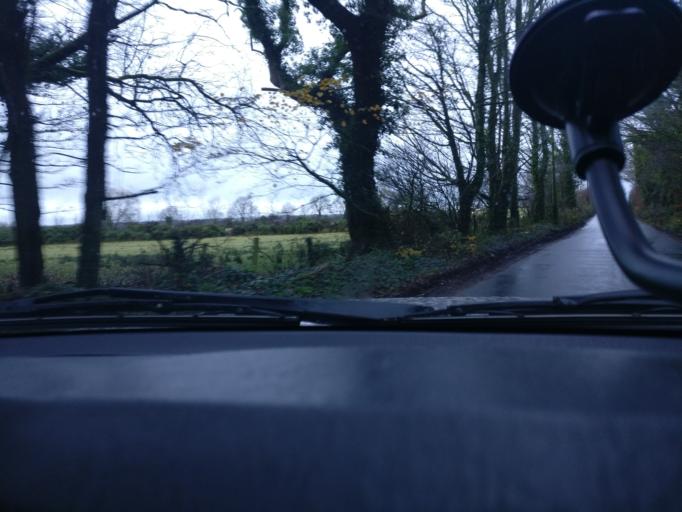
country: IE
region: Connaught
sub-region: County Galway
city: Loughrea
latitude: 53.2496
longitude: -8.5798
